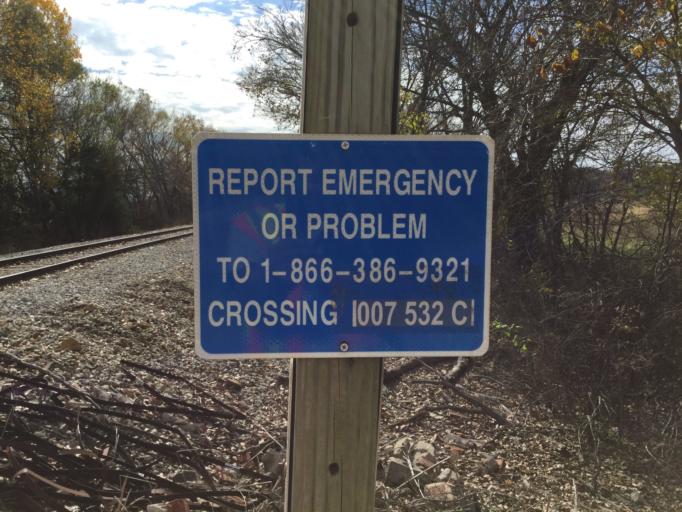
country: US
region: Kansas
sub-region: Montgomery County
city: Cherryvale
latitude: 37.2379
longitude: -95.5579
